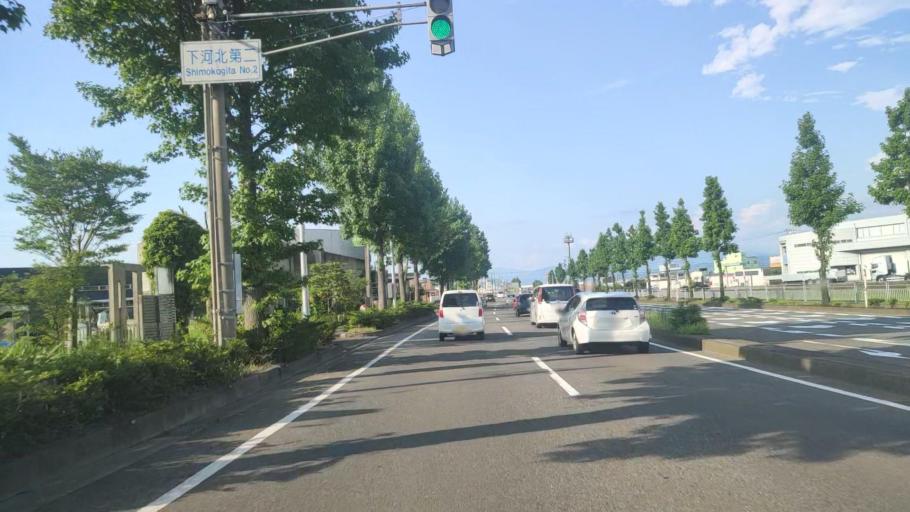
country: JP
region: Fukui
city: Fukui-shi
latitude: 36.0188
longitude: 136.2120
